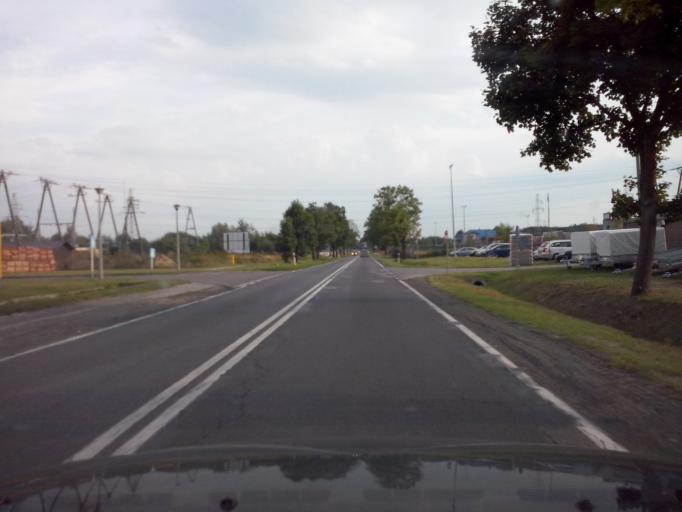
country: PL
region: Lublin Voivodeship
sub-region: Powiat bilgorajski
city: Bilgoraj
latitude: 50.5165
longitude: 22.7155
